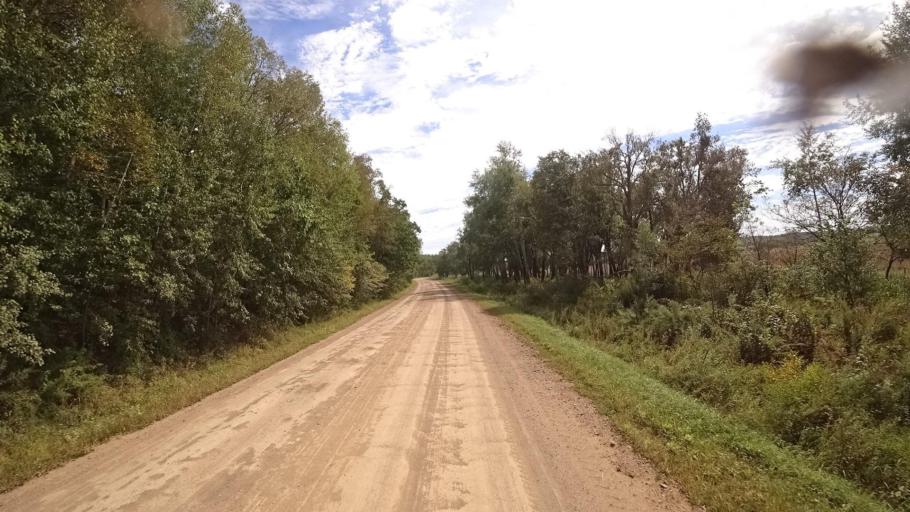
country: RU
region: Primorskiy
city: Yakovlevka
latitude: 44.5720
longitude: 133.5929
